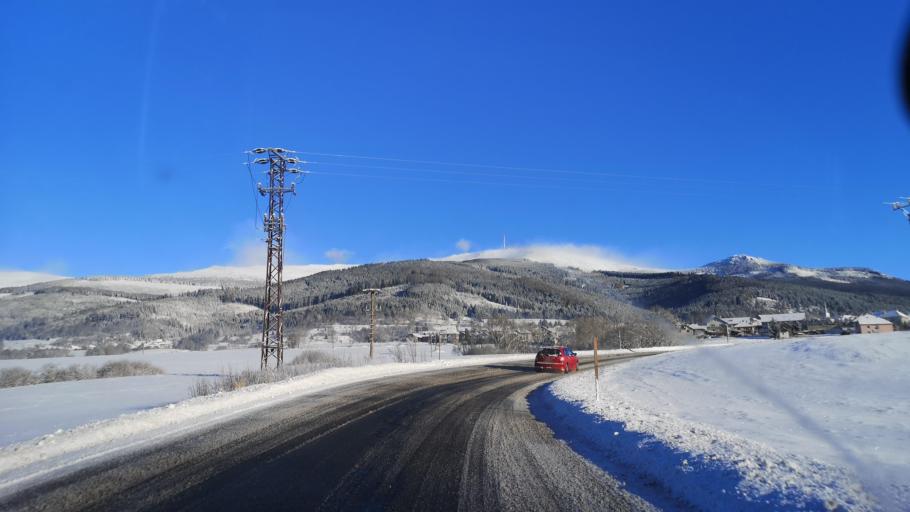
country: SK
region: Banskobystricky
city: Revuca
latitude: 48.8325
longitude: 20.1230
